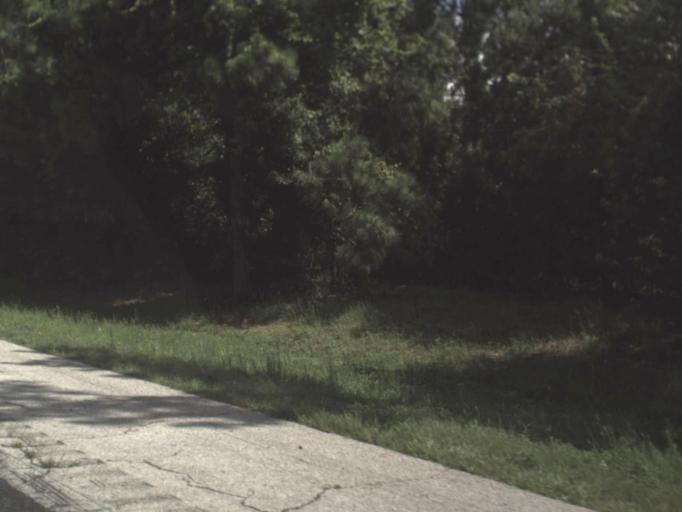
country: US
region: Florida
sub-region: Alachua County
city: Gainesville
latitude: 29.6503
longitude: -82.4108
